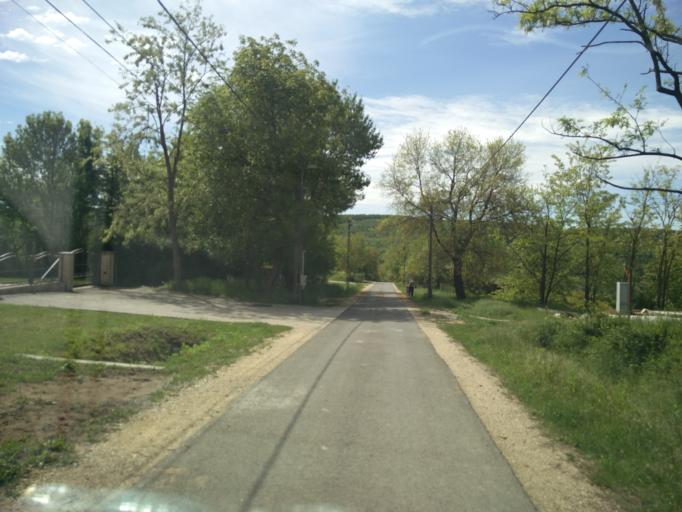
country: HU
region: Tolna
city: Szentgalpuszta
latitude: 46.2789
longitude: 18.6371
